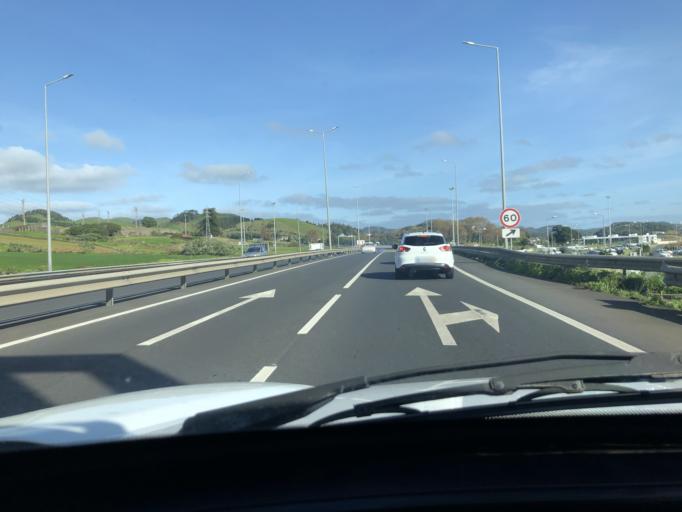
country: PT
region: Azores
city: Ponta Delgada
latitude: 37.7535
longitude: -25.6781
